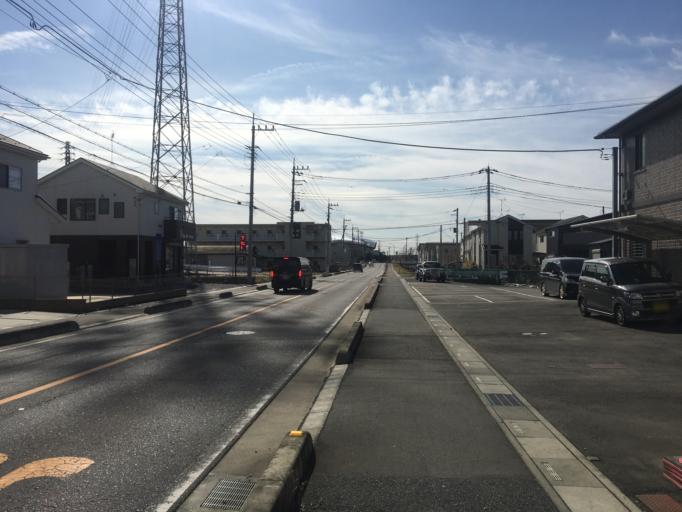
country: JP
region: Saitama
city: Sakado
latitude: 35.9955
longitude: 139.4013
